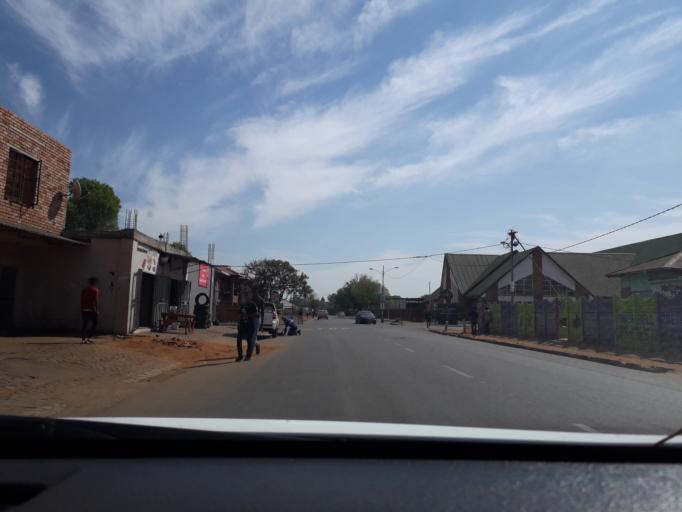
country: ZA
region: Gauteng
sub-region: City of Johannesburg Metropolitan Municipality
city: Modderfontein
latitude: -26.1053
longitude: 28.2378
